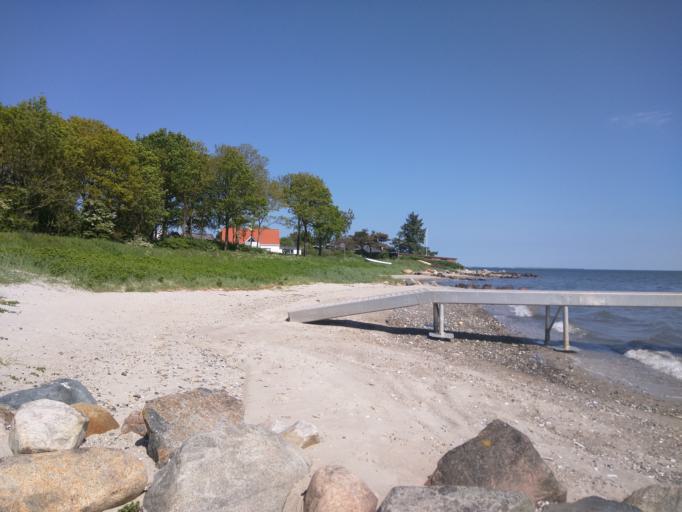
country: DK
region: North Denmark
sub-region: Morso Kommune
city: Nykobing Mors
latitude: 56.8000
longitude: 8.8778
